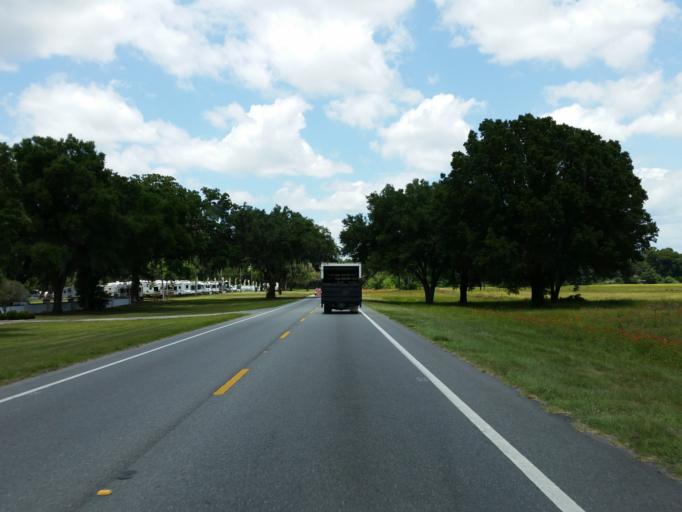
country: US
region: Florida
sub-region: Marion County
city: Belleview
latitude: 28.9991
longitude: -82.0413
